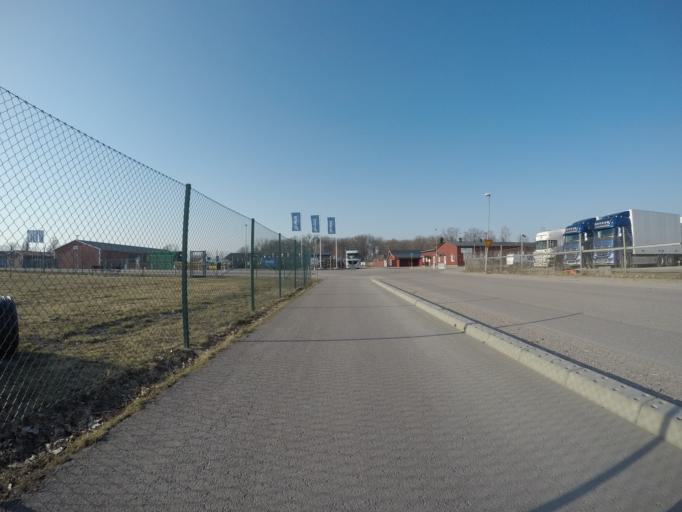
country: SE
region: Vaestmanland
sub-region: Kungsors Kommun
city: Kungsoer
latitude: 59.4291
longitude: 16.1120
